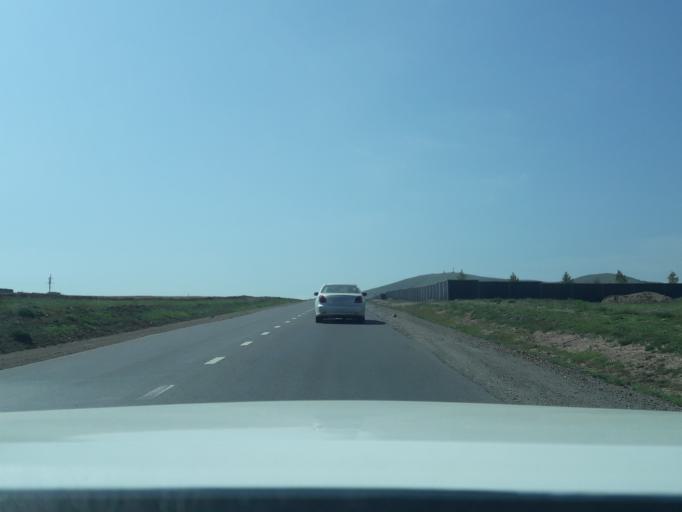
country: MN
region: Ulaanbaatar
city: Ulaanbaatar
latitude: 47.8054
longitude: 106.7494
